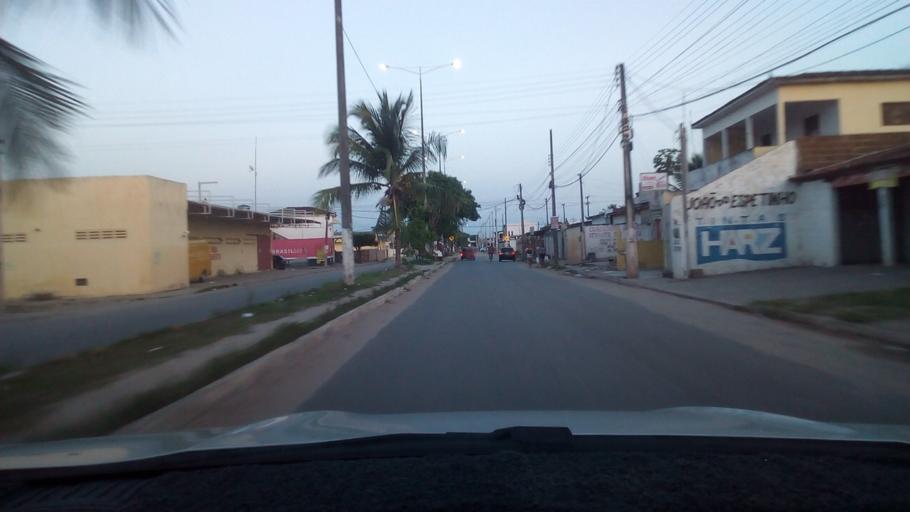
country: BR
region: Paraiba
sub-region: Bayeux
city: Bayeux
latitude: -7.1760
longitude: -34.9264
